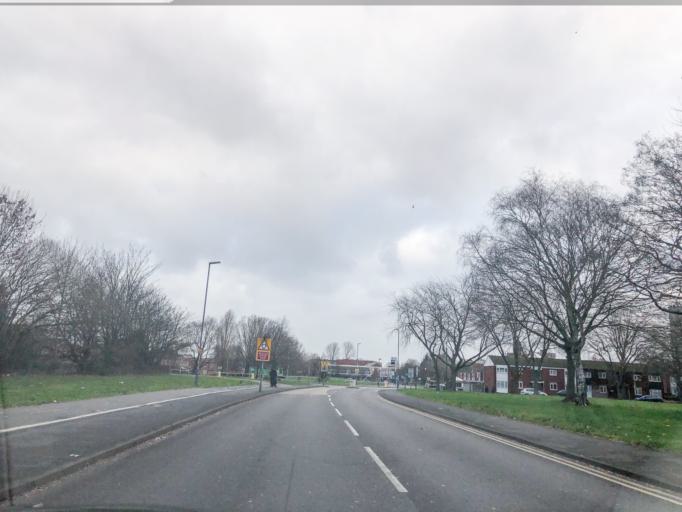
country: GB
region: England
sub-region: City and Borough of Birmingham
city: Birmingham
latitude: 52.4620
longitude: -1.8946
